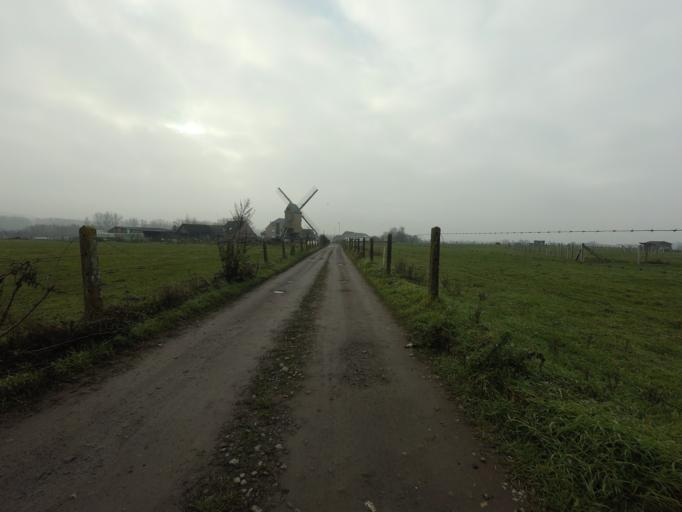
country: BE
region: Flanders
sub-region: Provincie Oost-Vlaanderen
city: Ninove
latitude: 50.8194
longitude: 3.9804
